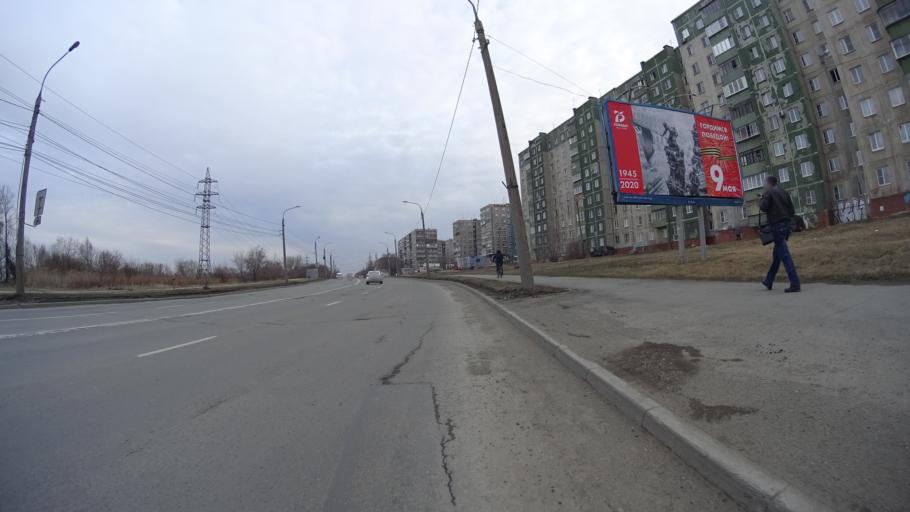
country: RU
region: Chelyabinsk
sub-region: Gorod Chelyabinsk
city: Chelyabinsk
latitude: 55.1858
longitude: 61.4845
